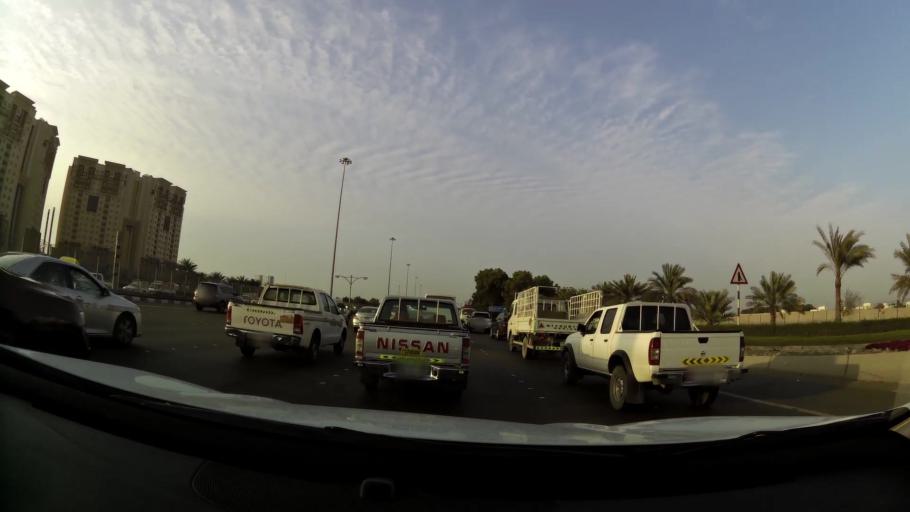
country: AE
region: Abu Dhabi
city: Abu Dhabi
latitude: 24.3831
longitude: 54.5246
